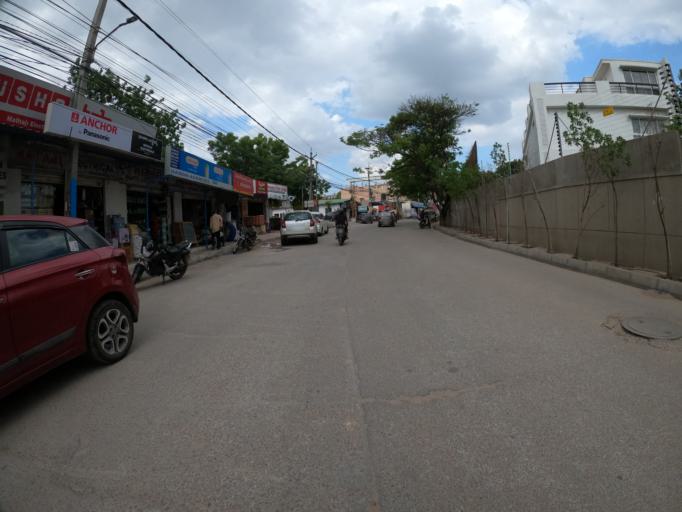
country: IN
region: Telangana
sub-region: Hyderabad
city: Hyderabad
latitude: 17.4073
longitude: 78.3861
